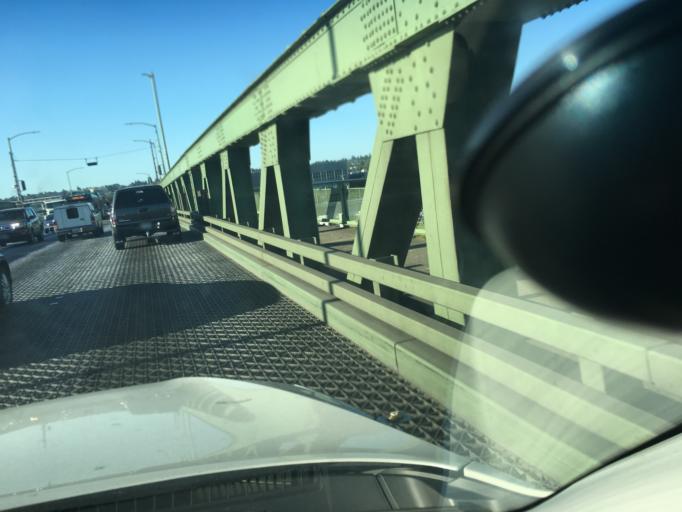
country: US
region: Washington
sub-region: King County
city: Seattle
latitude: 47.6595
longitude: -122.3762
